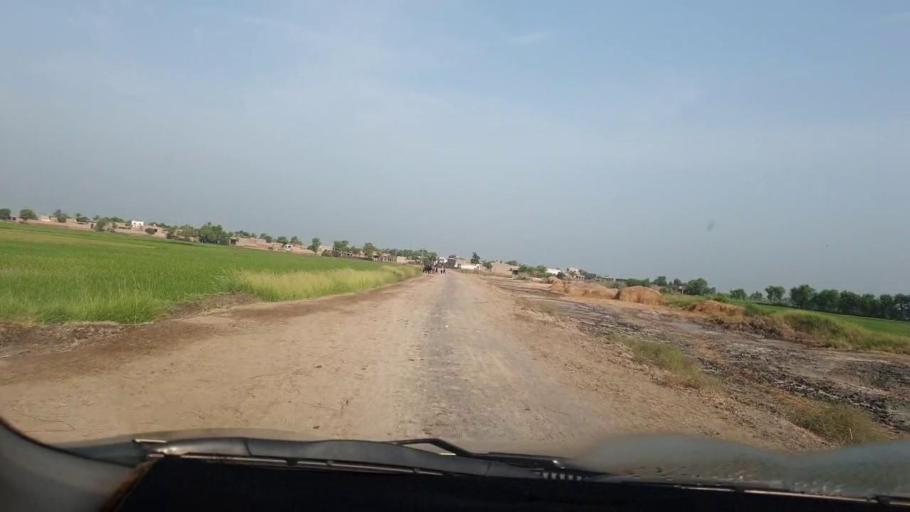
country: PK
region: Sindh
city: Goth Garelo
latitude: 27.4859
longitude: 68.0700
